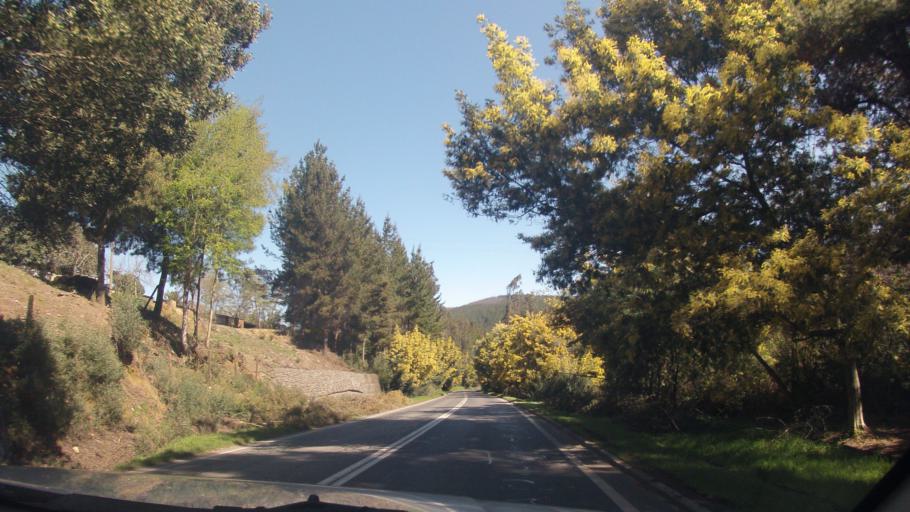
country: CL
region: Araucania
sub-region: Provincia de Malleco
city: Traiguen
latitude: -38.1751
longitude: -72.9411
